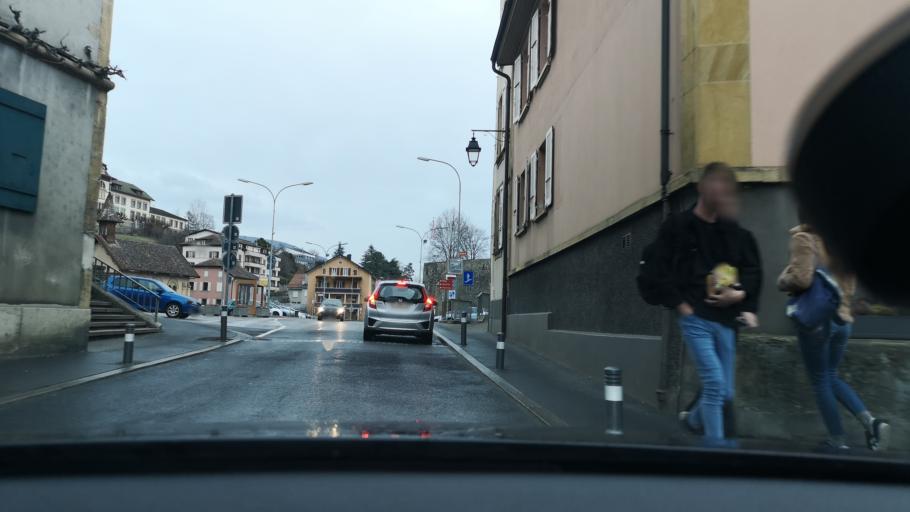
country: CH
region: Vaud
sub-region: Jura-Nord vaudois District
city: Grandson
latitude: 46.8089
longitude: 6.6454
